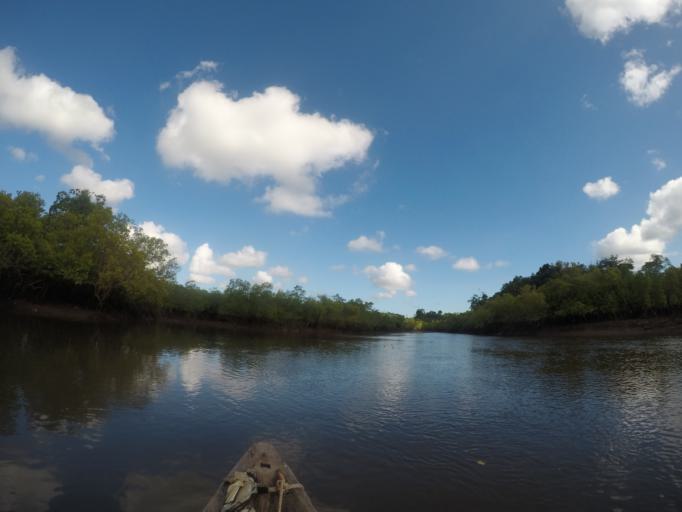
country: TZ
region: Pemba South
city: Mtambile
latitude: -5.3438
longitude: 39.6925
